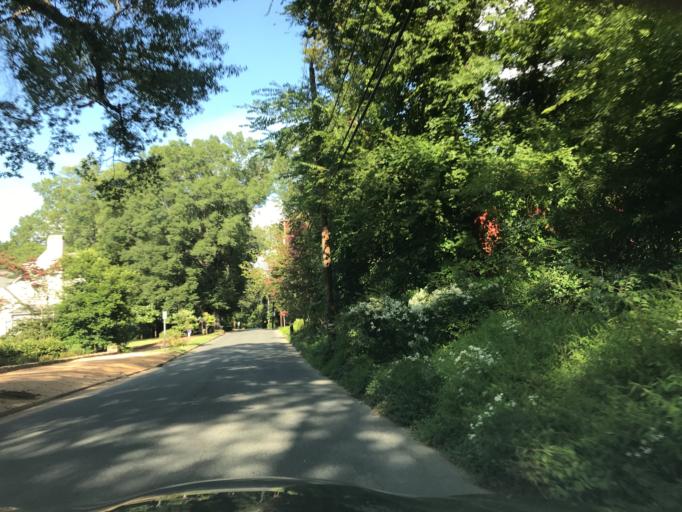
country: US
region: North Carolina
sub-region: Orange County
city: Chapel Hill
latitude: 35.9175
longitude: -79.0474
